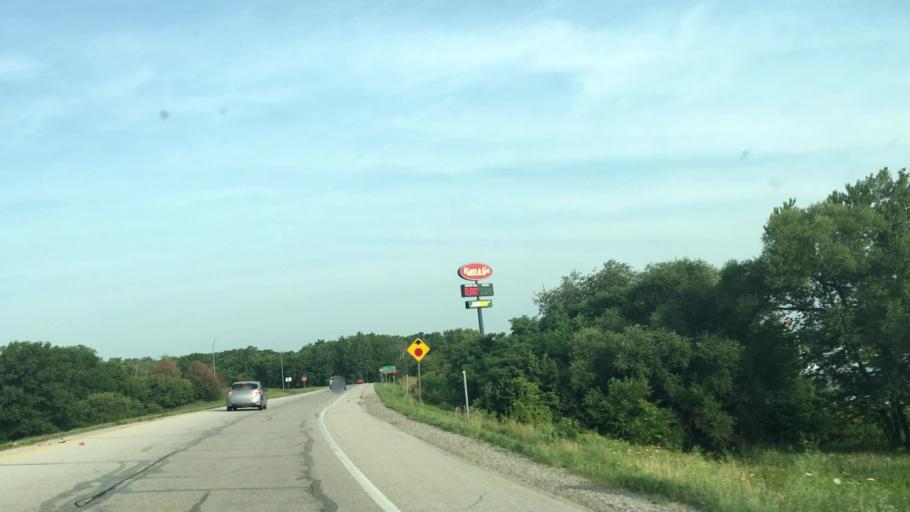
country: US
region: Iowa
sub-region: Johnson County
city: Tiffin
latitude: 41.6943
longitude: -91.6637
